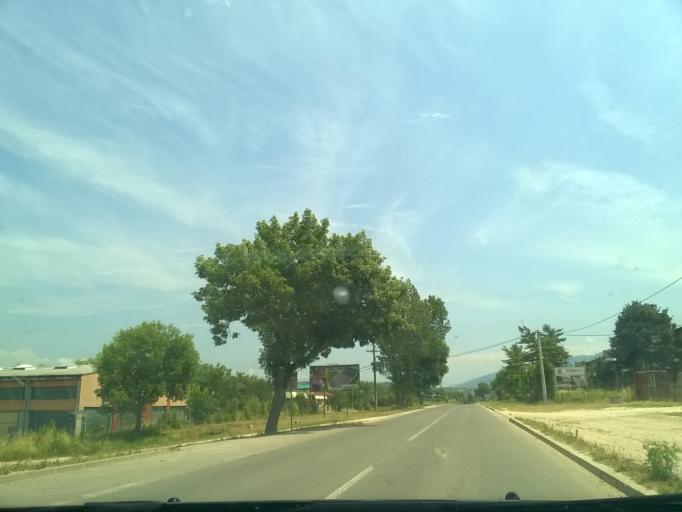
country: RS
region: Central Serbia
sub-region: Zajecarski Okrug
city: Soko Banja
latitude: 43.6520
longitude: 21.8486
